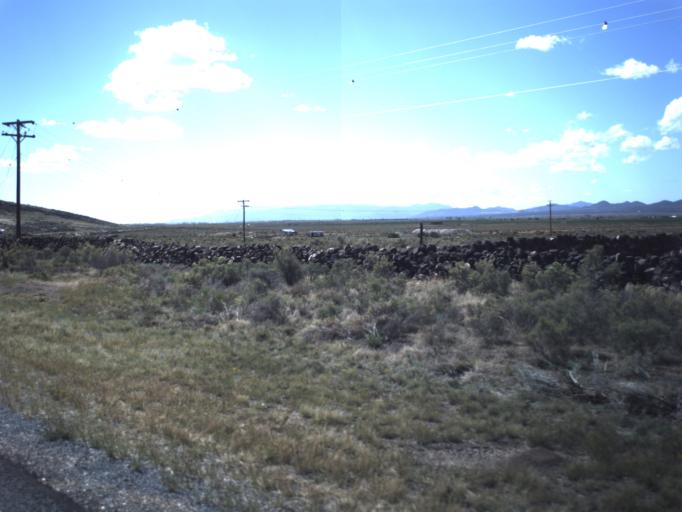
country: US
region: Utah
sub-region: Iron County
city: Enoch
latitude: 37.8571
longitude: -113.0317
